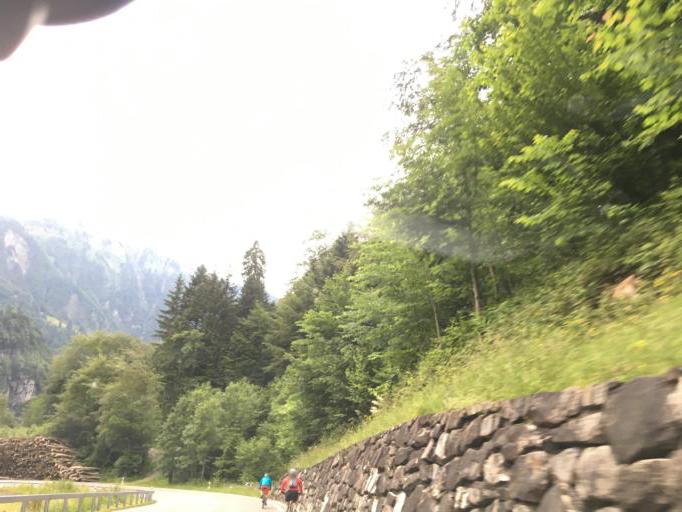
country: CH
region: Obwalden
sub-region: Obwalden
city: Engelberg
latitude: 46.8462
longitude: 8.3758
